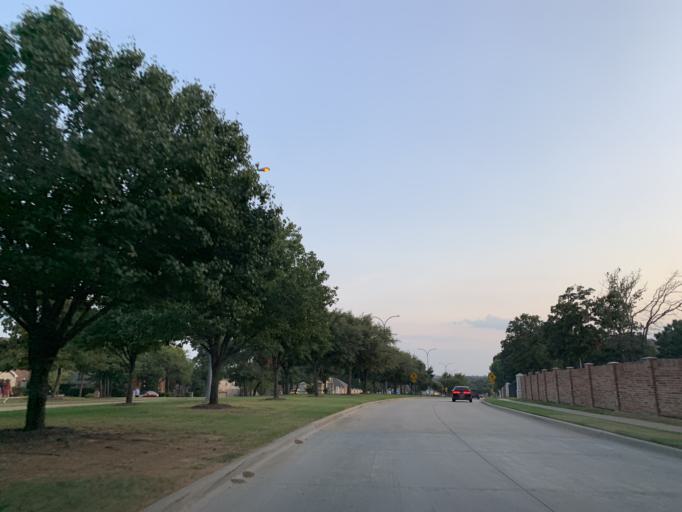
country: US
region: Texas
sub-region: Tarrant County
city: Keller
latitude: 32.9510
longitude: -97.2653
